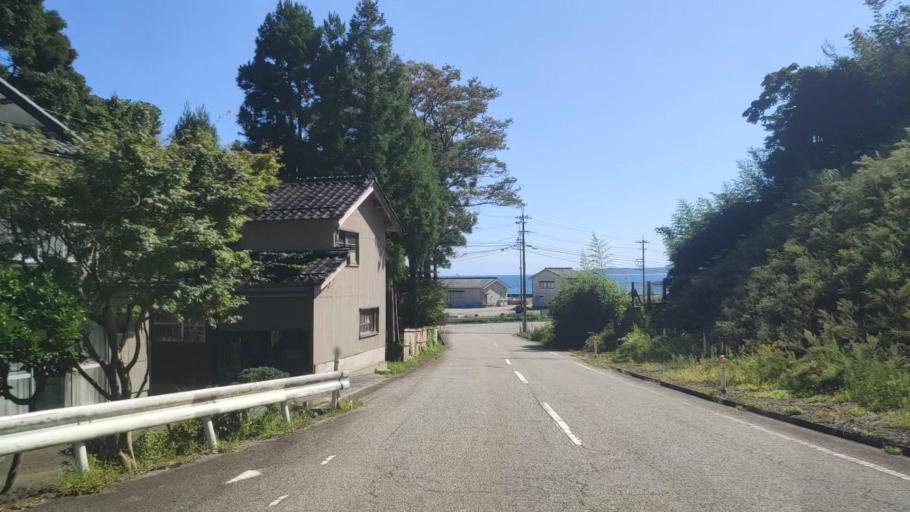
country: JP
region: Toyama
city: Nyuzen
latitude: 37.5027
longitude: 137.3494
